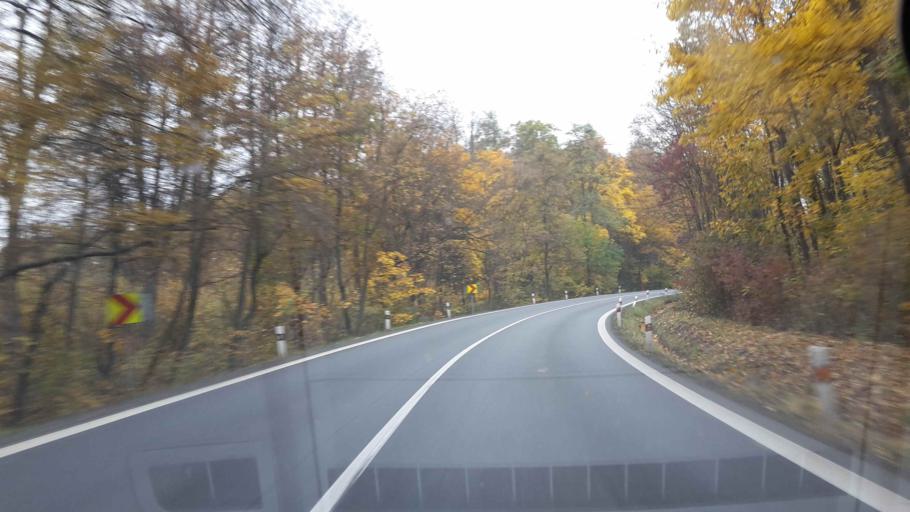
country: CZ
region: South Moravian
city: Damborice
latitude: 49.0828
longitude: 16.9307
